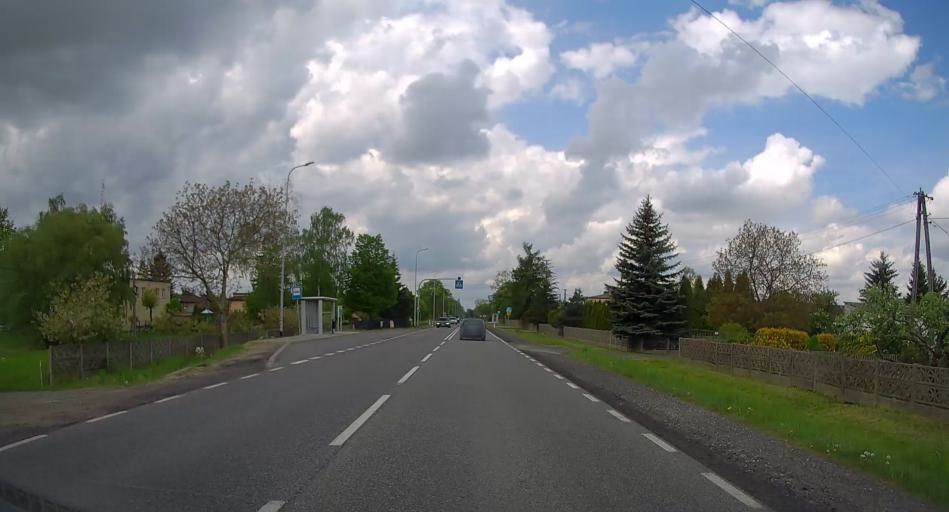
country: PL
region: Masovian Voivodeship
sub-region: Powiat plonski
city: Zaluski
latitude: 52.4454
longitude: 20.5149
